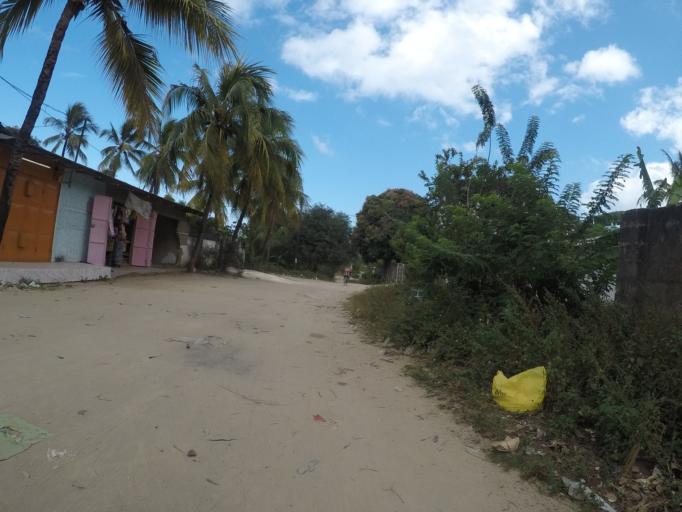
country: TZ
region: Zanzibar Urban/West
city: Zanzibar
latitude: -6.1873
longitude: 39.2166
